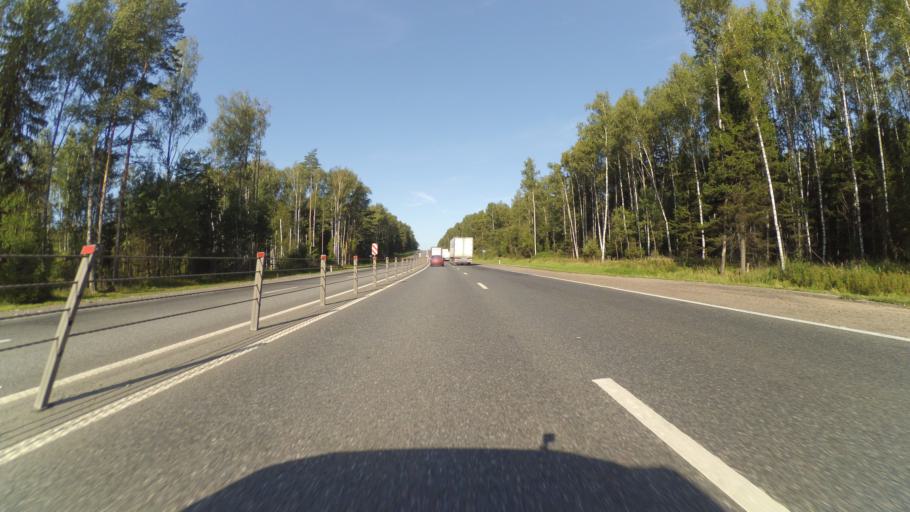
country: RU
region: Moskovskaya
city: Uvarovka
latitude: 55.4913
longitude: 35.3987
